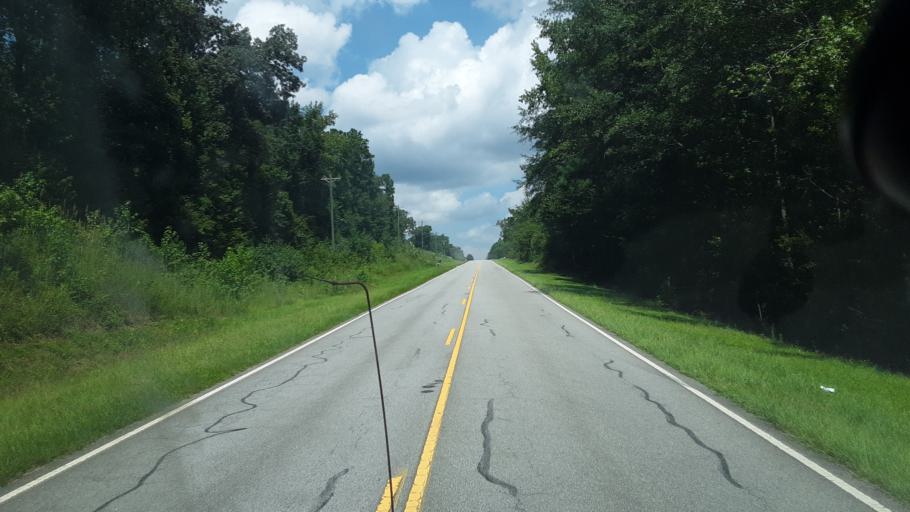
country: US
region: South Carolina
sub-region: Calhoun County
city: Oak Grove
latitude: 33.7411
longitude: -80.9593
